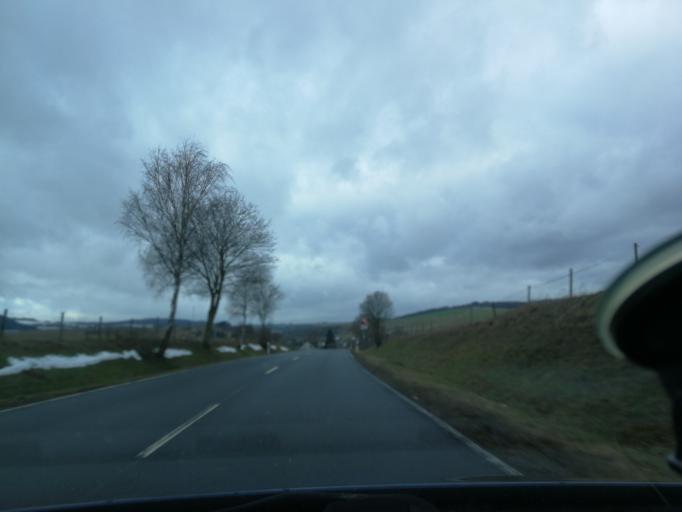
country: DE
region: Rheinland-Pfalz
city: Dreis-Bruck
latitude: 50.2589
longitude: 6.7994
